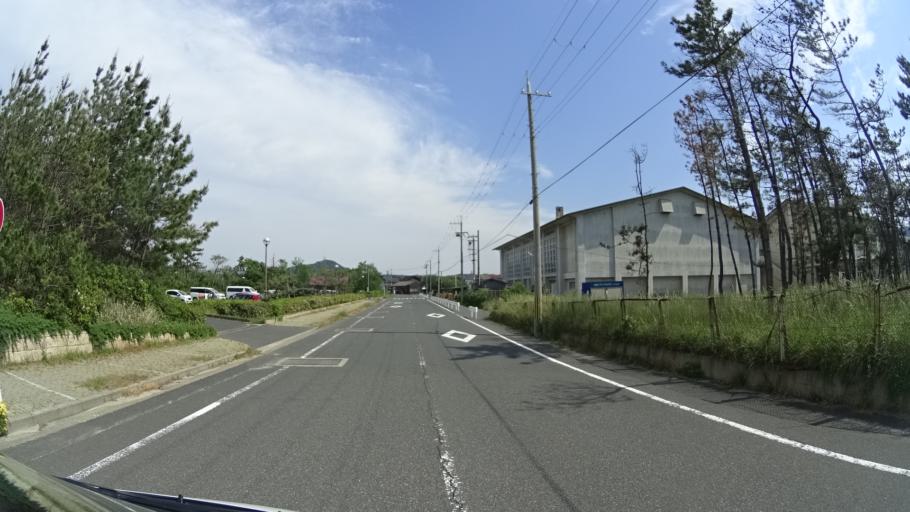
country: JP
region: Kyoto
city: Miyazu
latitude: 35.6901
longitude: 135.0286
